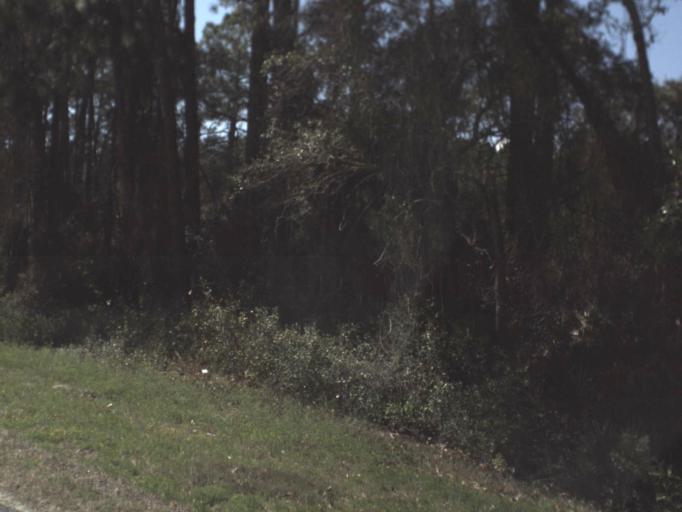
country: US
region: Florida
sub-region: Franklin County
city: Carrabelle
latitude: 29.9107
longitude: -84.5362
